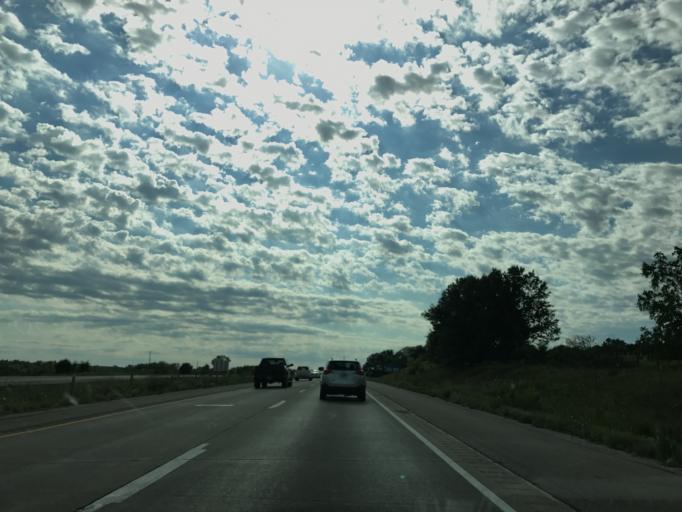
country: US
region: Iowa
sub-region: Dallas County
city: Van Meter
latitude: 41.5446
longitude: -93.9740
